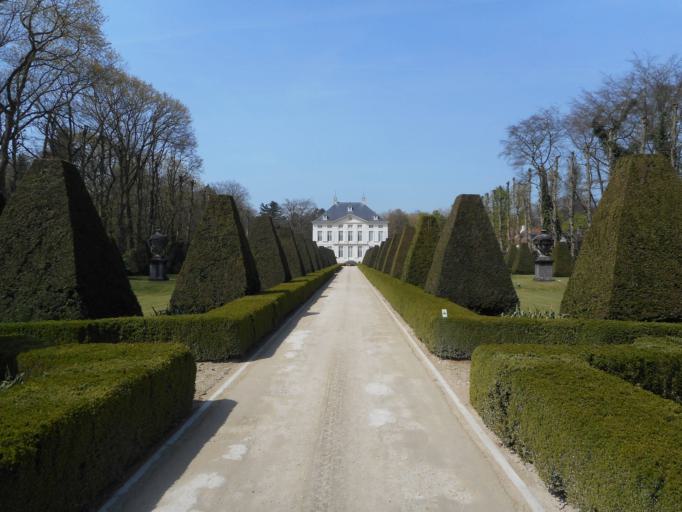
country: BE
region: Flanders
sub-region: Provincie Antwerpen
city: Zoersel
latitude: 51.2578
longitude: 4.7025
